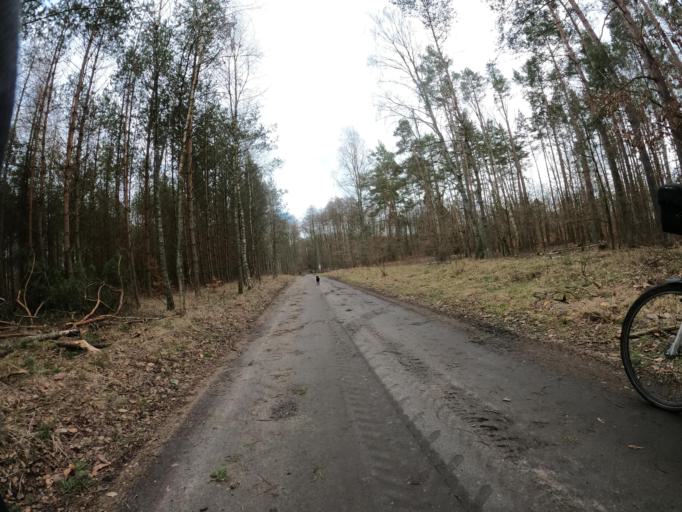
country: PL
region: Greater Poland Voivodeship
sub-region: Powiat zlotowski
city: Sypniewo
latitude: 53.4527
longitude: 16.5379
